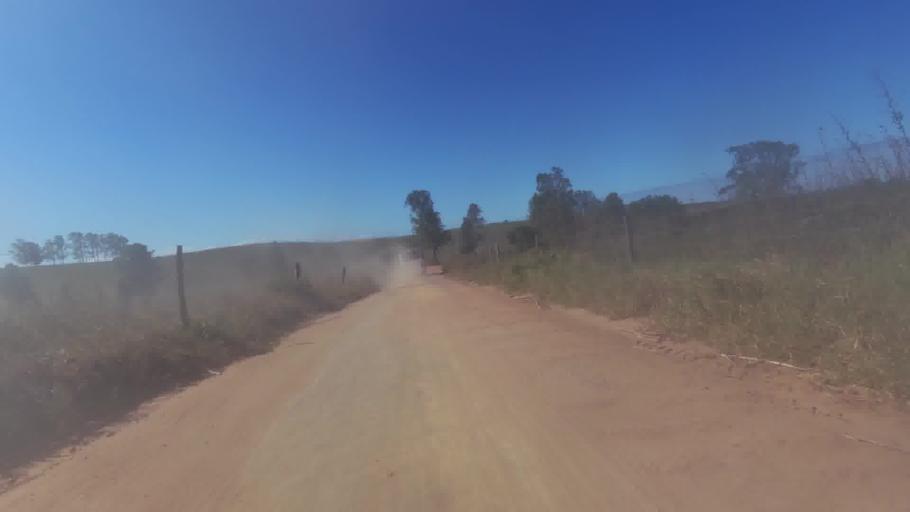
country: BR
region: Espirito Santo
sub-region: Marataizes
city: Marataizes
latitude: -21.1243
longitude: -40.9781
